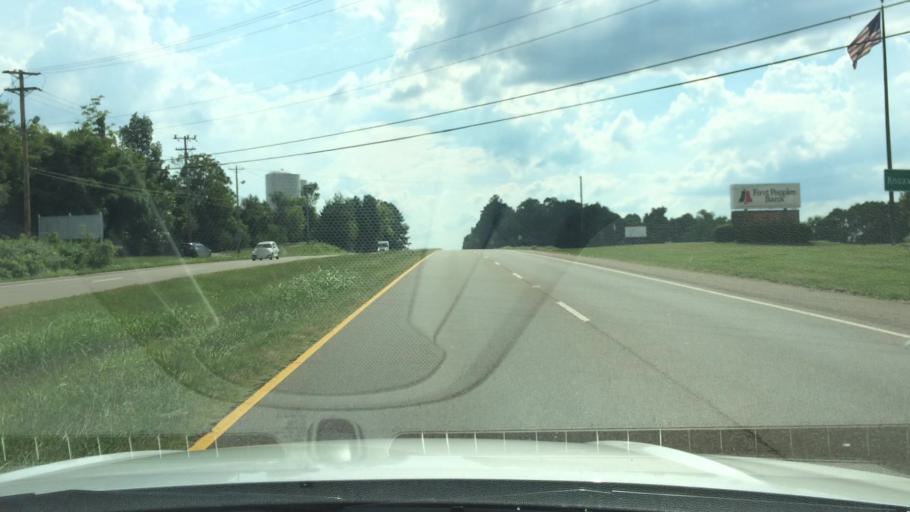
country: US
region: Tennessee
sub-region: Jefferson County
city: Jefferson City
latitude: 36.1133
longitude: -83.5009
